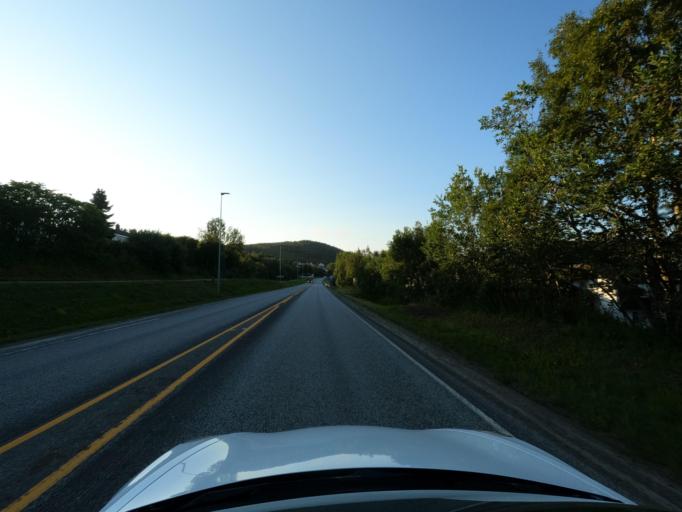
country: NO
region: Troms
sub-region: Harstad
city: Harstad
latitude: 68.7676
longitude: 16.5590
